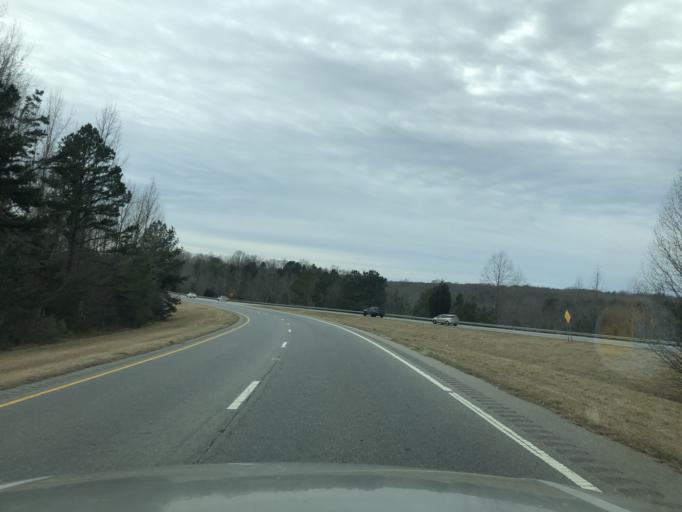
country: US
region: North Carolina
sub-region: Gaston County
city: Bessemer City
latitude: 35.2503
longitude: -81.3018
